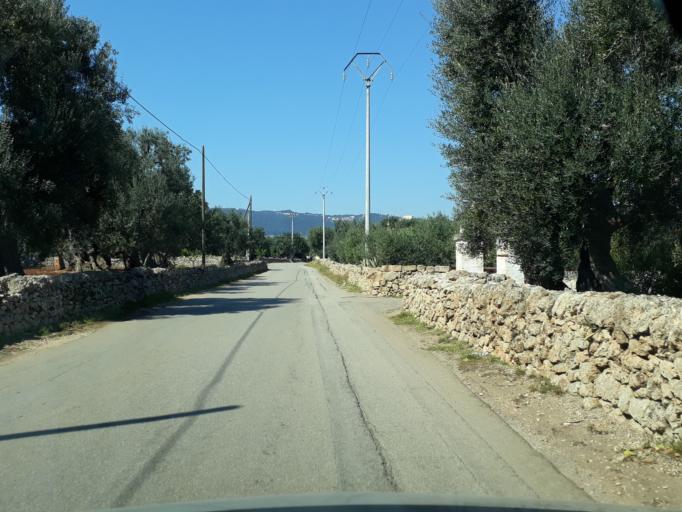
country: IT
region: Apulia
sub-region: Provincia di Brindisi
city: Fasano
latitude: 40.8352
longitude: 17.3749
